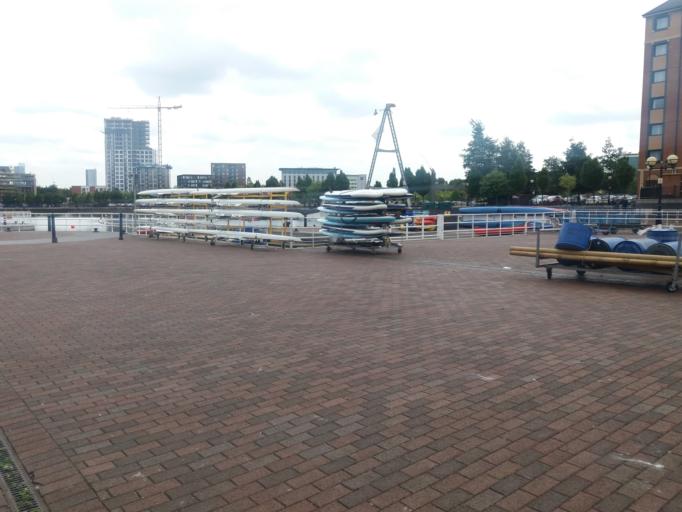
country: GB
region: England
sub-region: City and Borough of Salford
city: Salford
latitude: 53.4708
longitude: -2.2890
